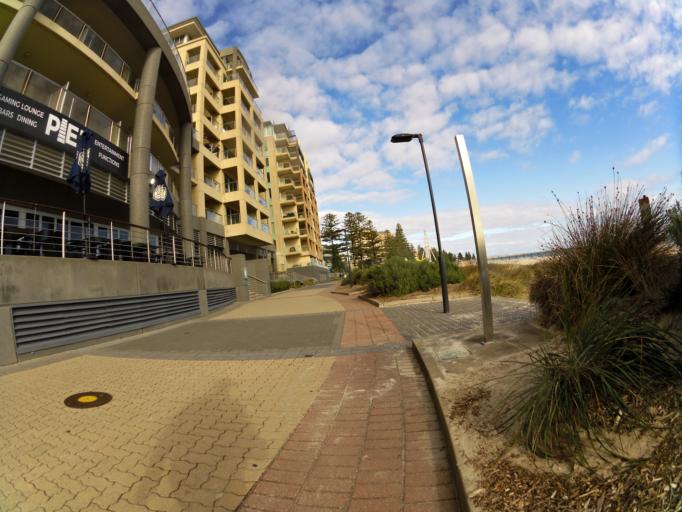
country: AU
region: South Australia
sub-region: Adelaide
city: Glenelg
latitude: -34.9775
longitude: 138.5105
